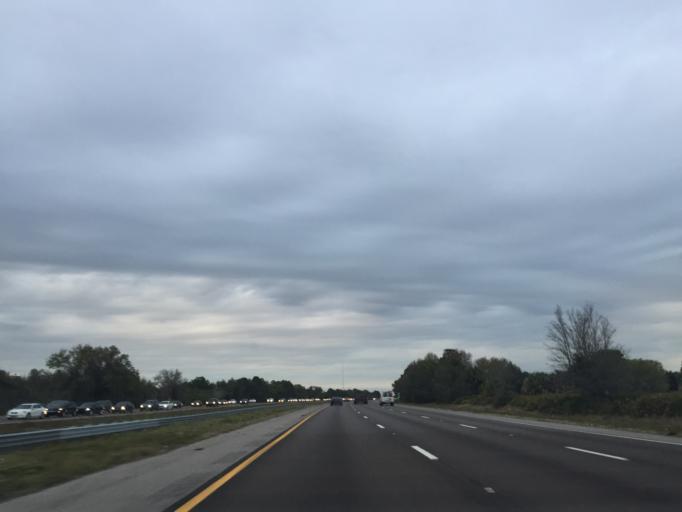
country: US
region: Florida
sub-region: Hillsborough County
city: Gibsonton
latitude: 27.8193
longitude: -82.3520
